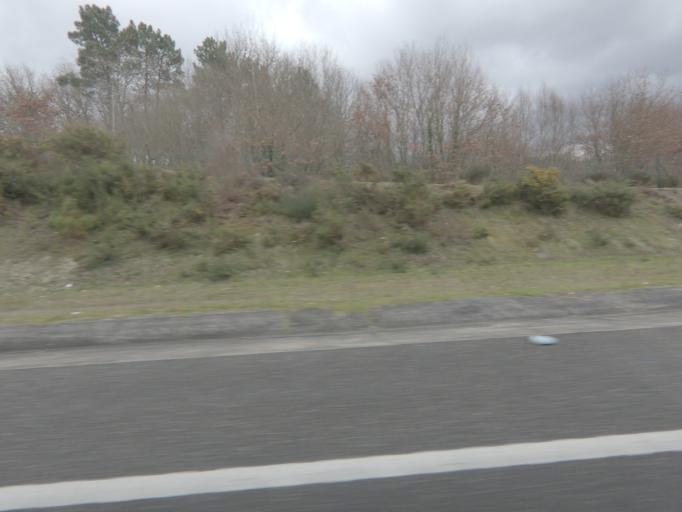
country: ES
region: Galicia
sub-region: Provincia de Ourense
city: Pinor
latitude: 42.4737
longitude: -8.0271
